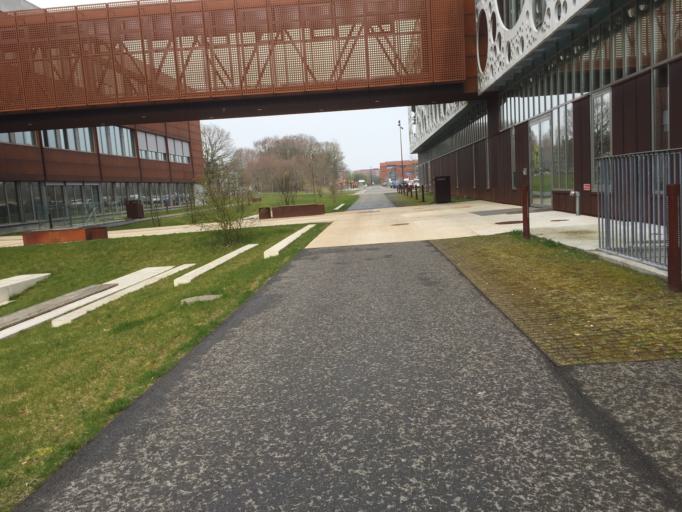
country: DK
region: South Denmark
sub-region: Odense Kommune
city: Neder Holluf
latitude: 55.3671
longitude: 10.4315
